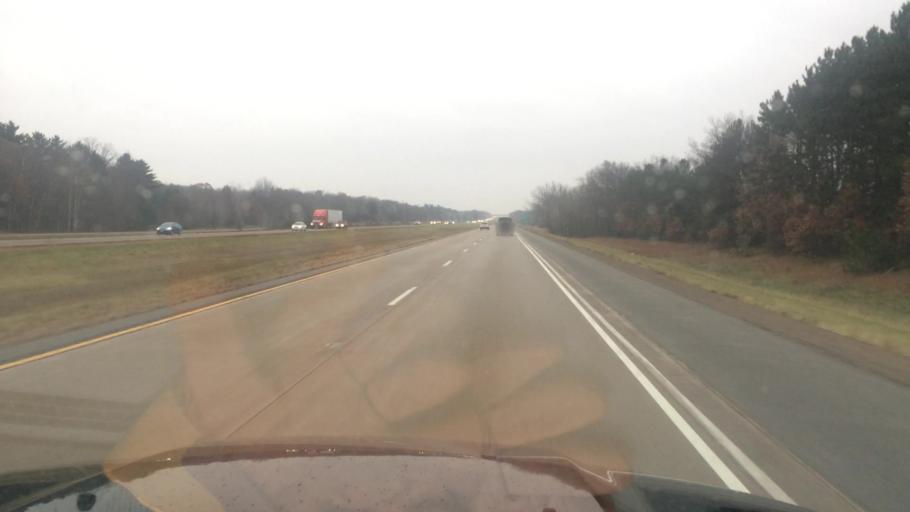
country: US
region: Wisconsin
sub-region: Portage County
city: Stevens Point
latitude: 44.6204
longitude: -89.6286
